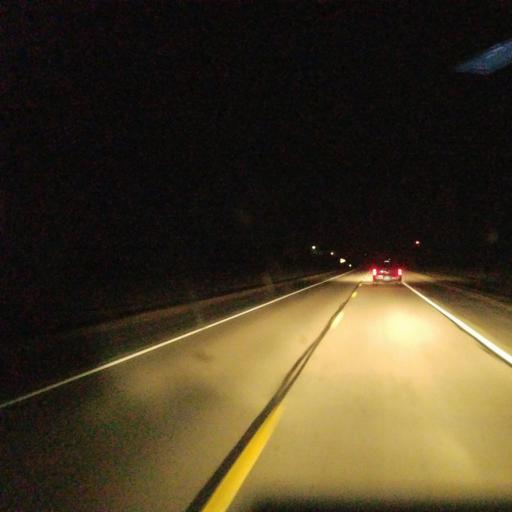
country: US
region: Illinois
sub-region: Knox County
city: Abingdon
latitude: 40.7292
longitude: -90.4332
